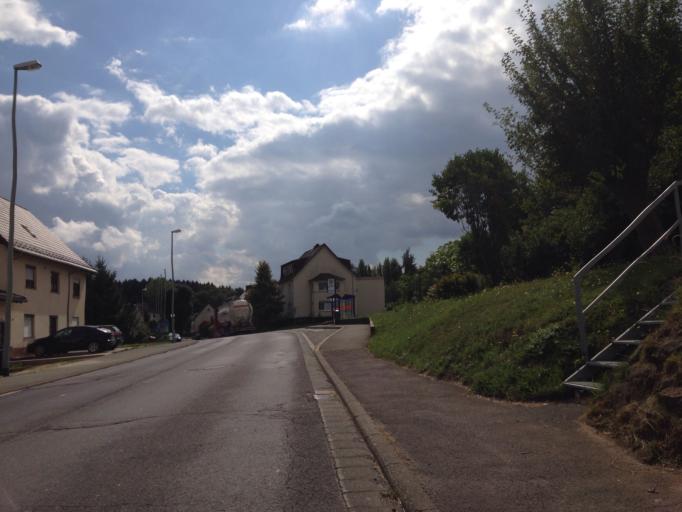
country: DE
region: Hesse
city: Mengerskirchen
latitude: 50.5608
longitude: 8.1531
